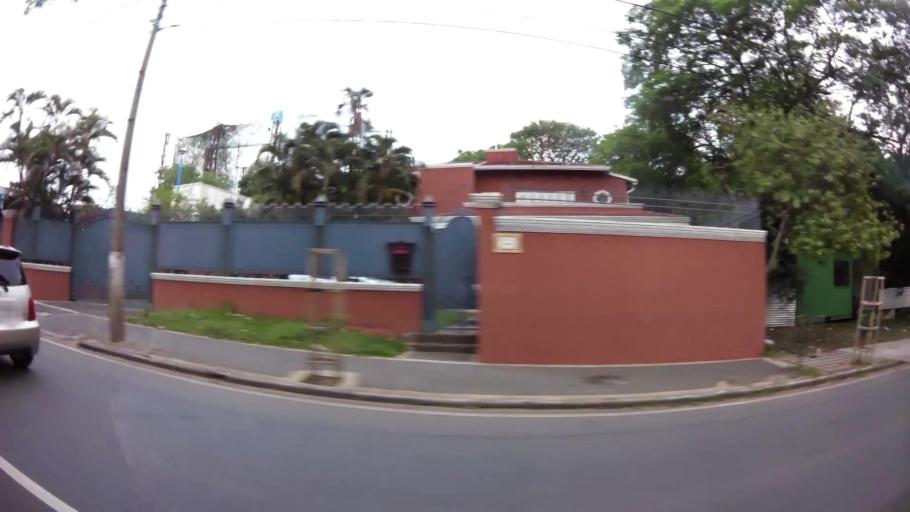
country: PY
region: Asuncion
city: Asuncion
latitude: -25.3242
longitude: -57.6242
